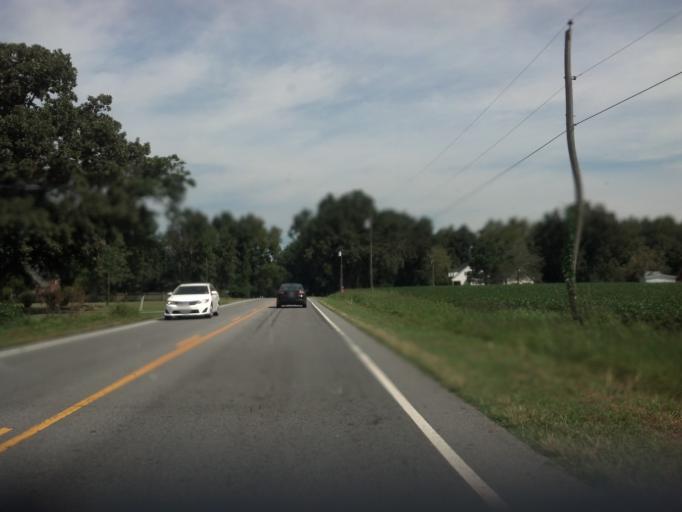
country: US
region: North Carolina
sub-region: Greene County
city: Maury
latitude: 35.5125
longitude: -77.6168
